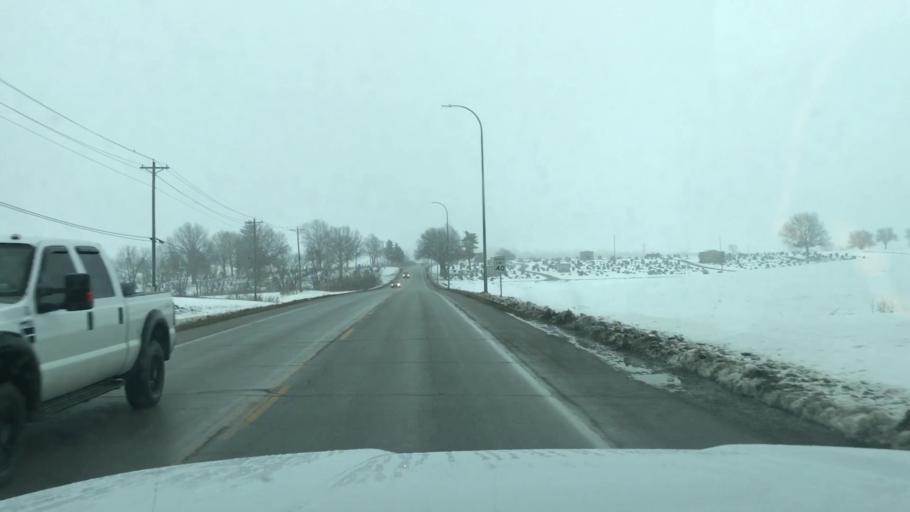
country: US
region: Missouri
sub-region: Clinton County
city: Cameron
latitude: 39.7318
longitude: -94.2293
